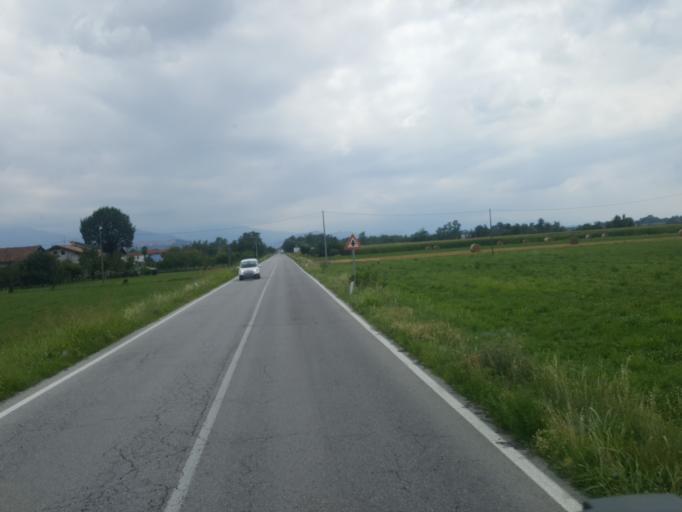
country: IT
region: Piedmont
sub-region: Provincia di Cuneo
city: Bastia Mondovi
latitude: 44.4373
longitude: 7.8676
